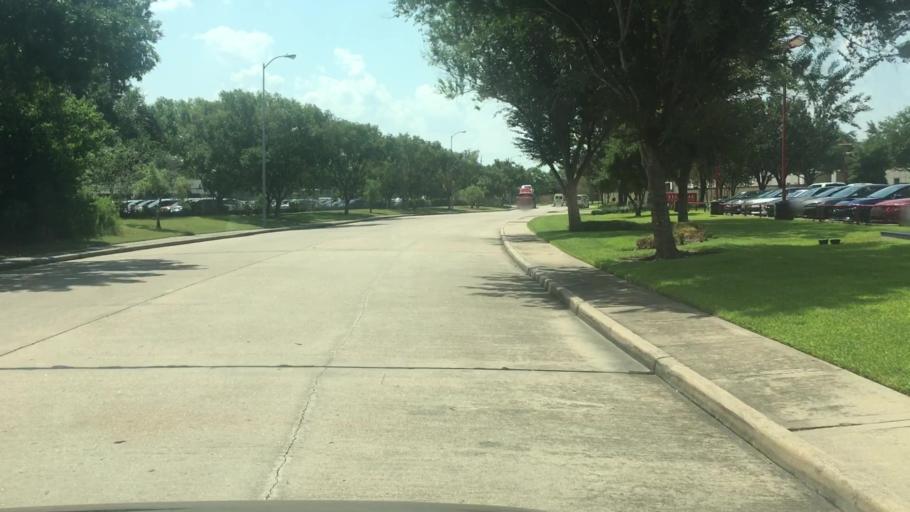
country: US
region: Texas
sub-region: Fort Bend County
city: Meadows Place
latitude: 29.6466
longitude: -95.5707
